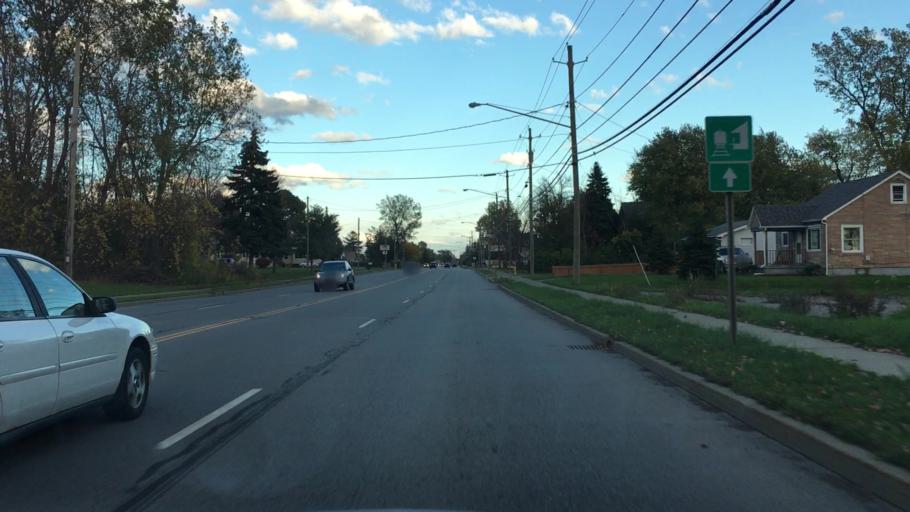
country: US
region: New York
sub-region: Erie County
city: Cheektowaga
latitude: 42.9039
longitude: -78.7416
